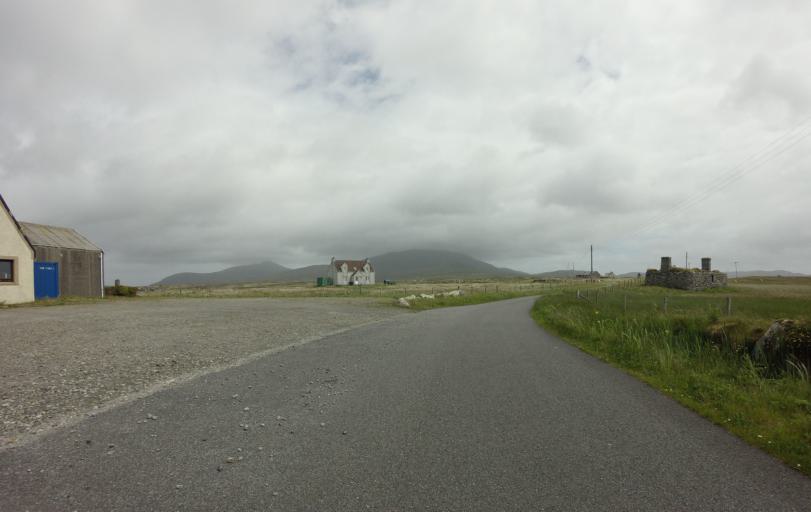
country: GB
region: Scotland
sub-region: Eilean Siar
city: Isle of South Uist
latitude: 57.2717
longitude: -7.3937
